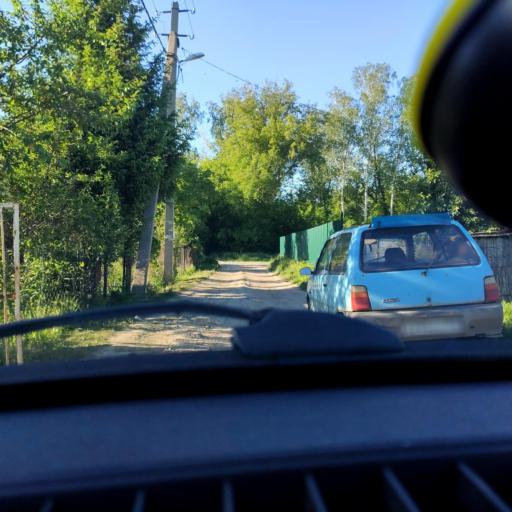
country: RU
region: Samara
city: Tol'yatti
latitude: 53.5976
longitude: 49.3154
